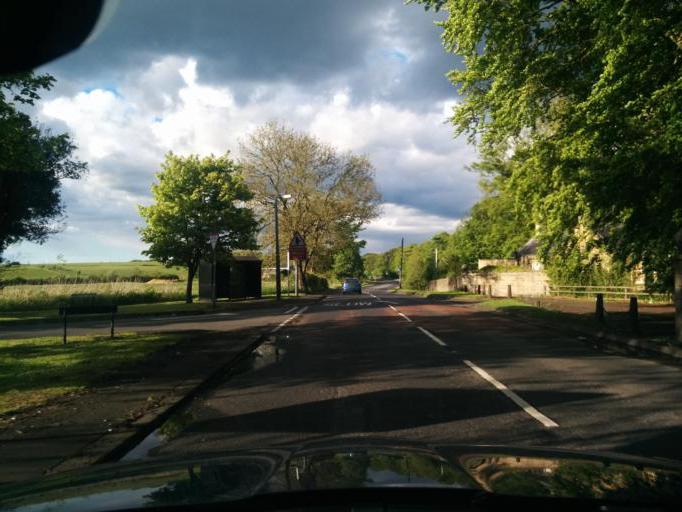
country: GB
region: England
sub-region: Northumberland
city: Bedlington
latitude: 55.1158
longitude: -1.6208
